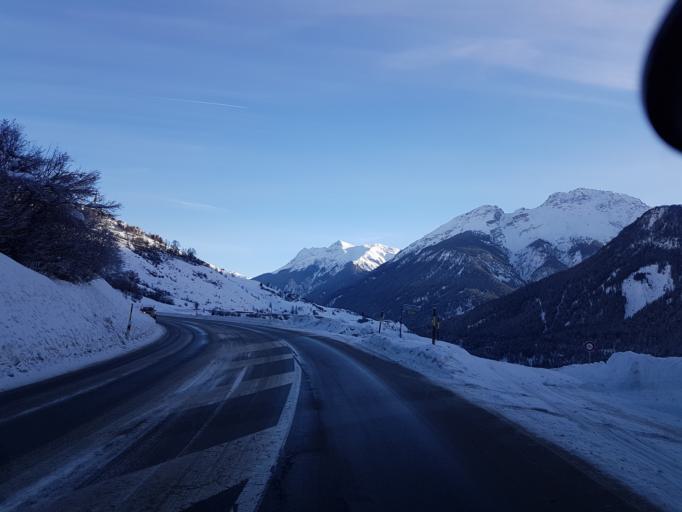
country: CH
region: Grisons
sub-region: Inn District
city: Scuol
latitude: 46.8078
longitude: 10.3248
